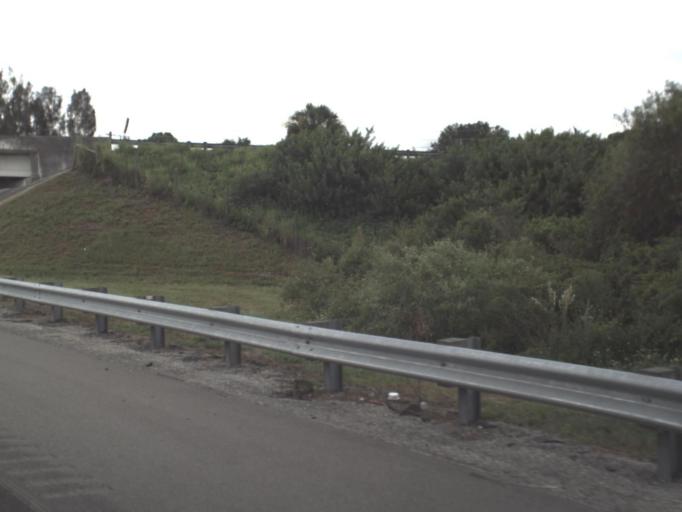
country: US
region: Florida
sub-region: Sarasota County
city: Nokomis
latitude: 27.1234
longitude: -82.3981
